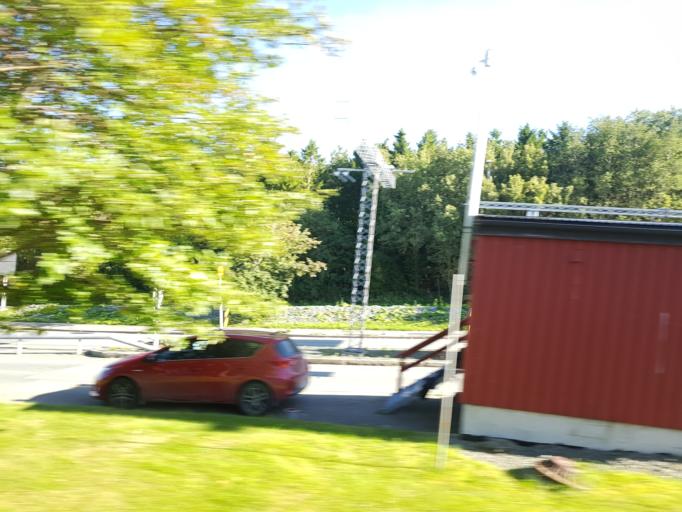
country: NO
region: Sor-Trondelag
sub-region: Skaun
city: Borsa
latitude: 63.4498
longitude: 10.1951
